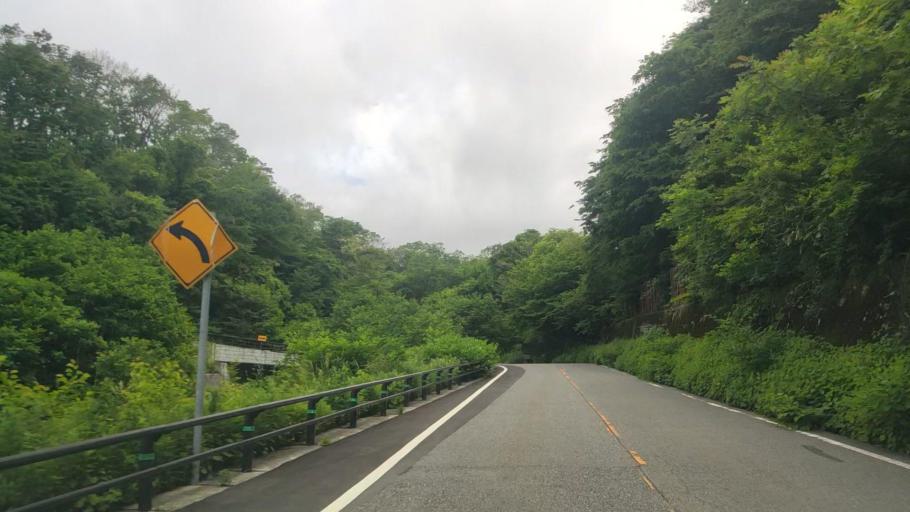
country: JP
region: Tottori
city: Yonago
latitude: 35.3377
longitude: 133.5582
